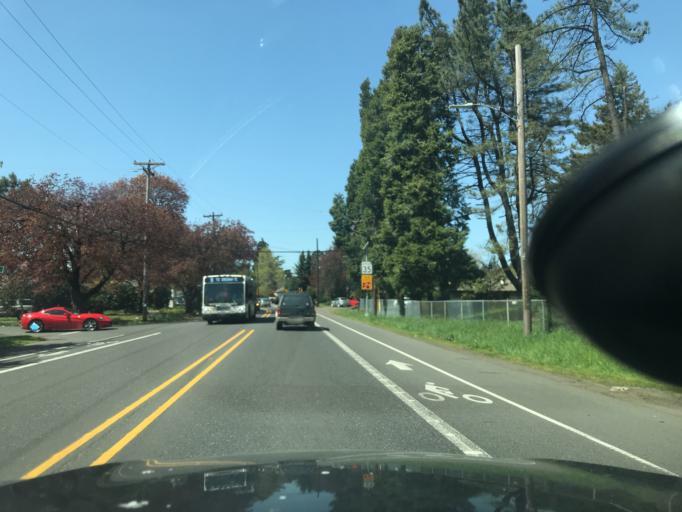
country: US
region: Oregon
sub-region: Clackamas County
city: Happy Valley
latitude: 45.4989
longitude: -122.5140
